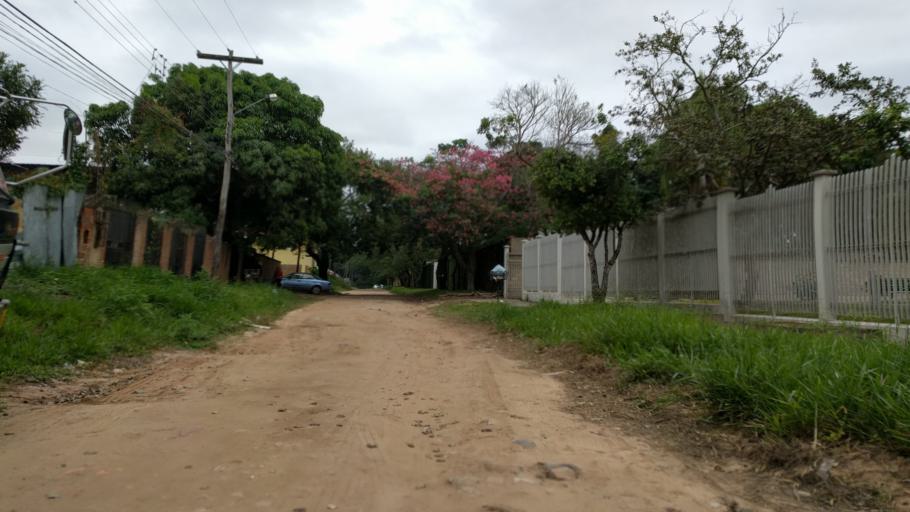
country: BO
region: Santa Cruz
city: Santa Cruz de la Sierra
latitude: -17.8077
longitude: -63.2197
